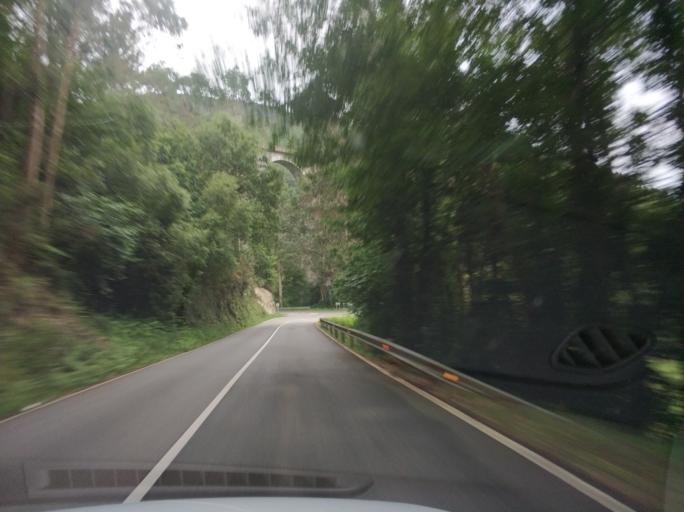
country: ES
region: Asturias
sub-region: Province of Asturias
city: Cudillero
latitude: 43.5535
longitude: -6.1910
